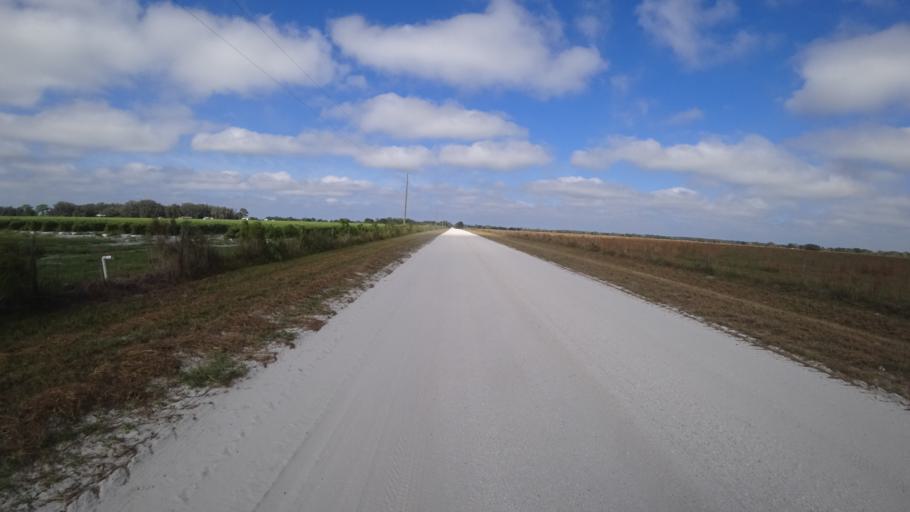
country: US
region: Florida
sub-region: DeSoto County
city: Arcadia
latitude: 27.3067
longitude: -82.0811
